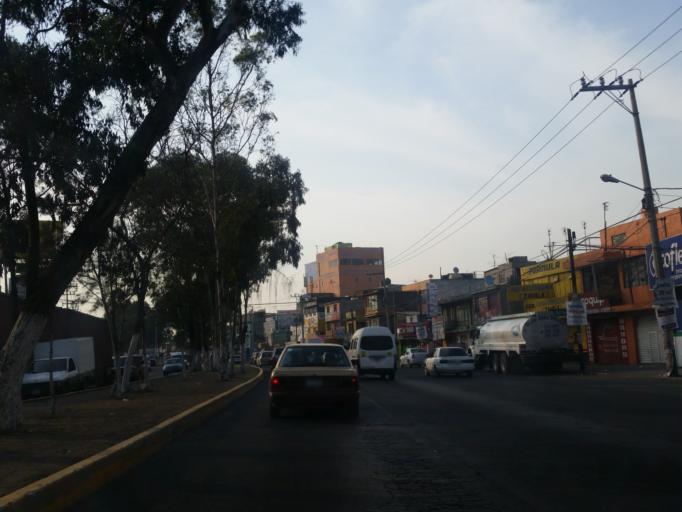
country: MX
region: Mexico
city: Los Reyes La Paz
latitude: 19.3551
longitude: -98.9787
